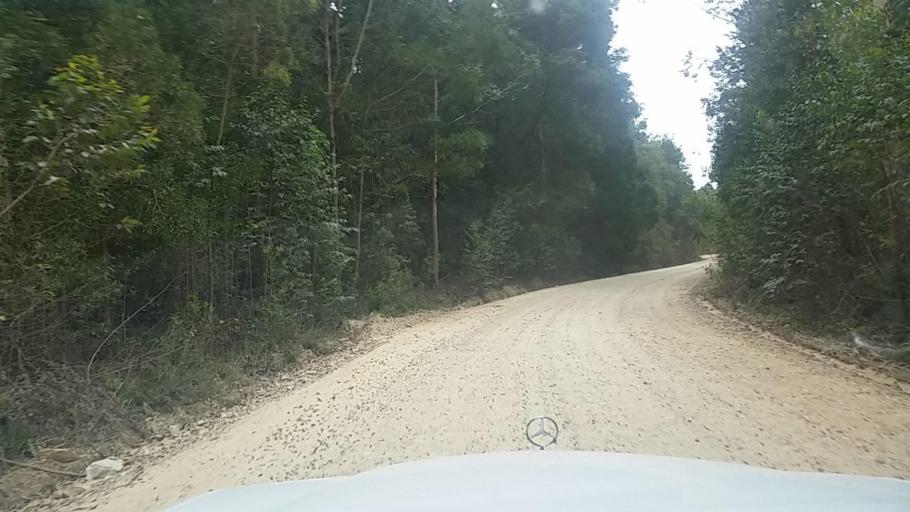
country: ZA
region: Western Cape
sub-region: Eden District Municipality
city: Knysna
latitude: -33.9981
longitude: 23.1268
